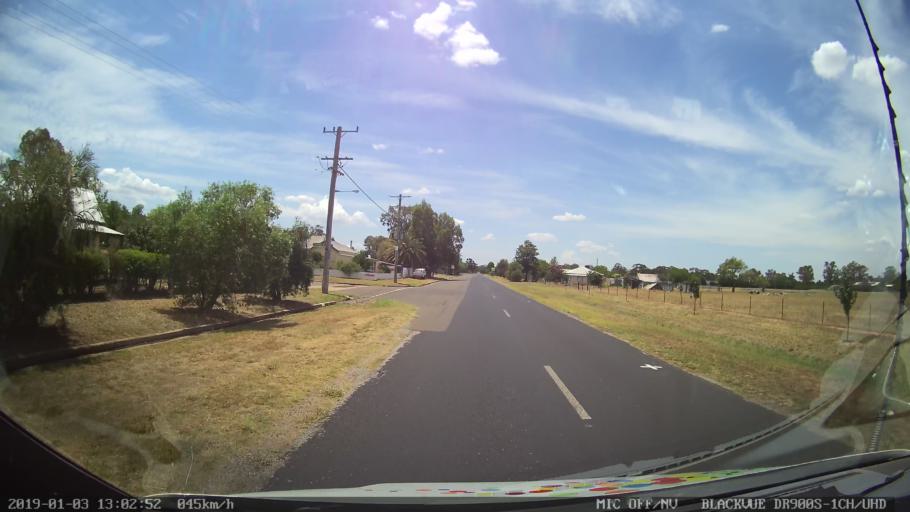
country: AU
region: New South Wales
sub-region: Cabonne
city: Canowindra
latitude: -33.6173
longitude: 148.4322
